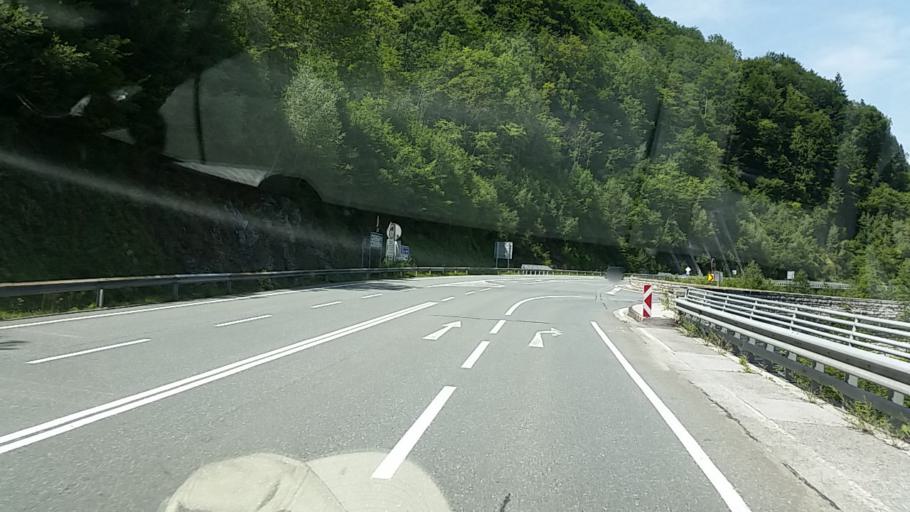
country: AT
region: Salzburg
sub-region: Politischer Bezirk Sankt Johann im Pongau
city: Bischofshofen
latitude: 47.4362
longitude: 13.2088
